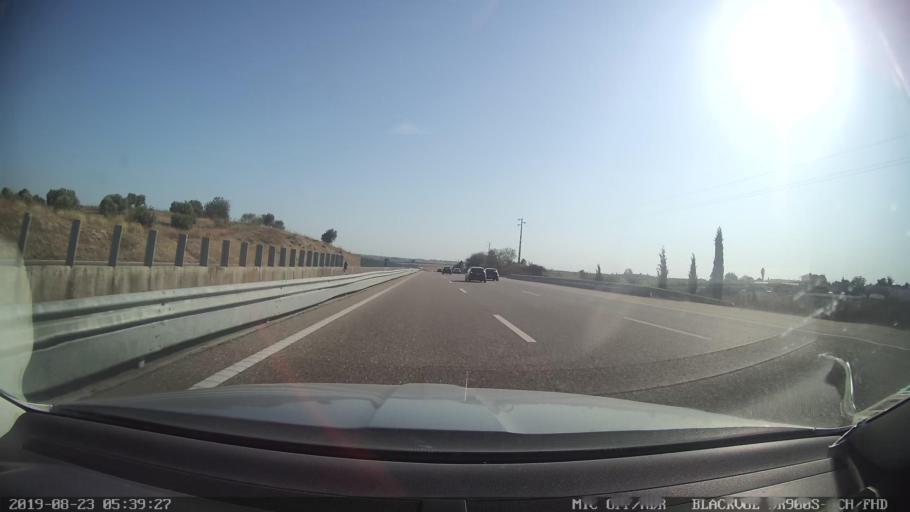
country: PT
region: Santarem
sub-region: Santarem
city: Santarem
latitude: 39.3057
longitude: -8.6772
